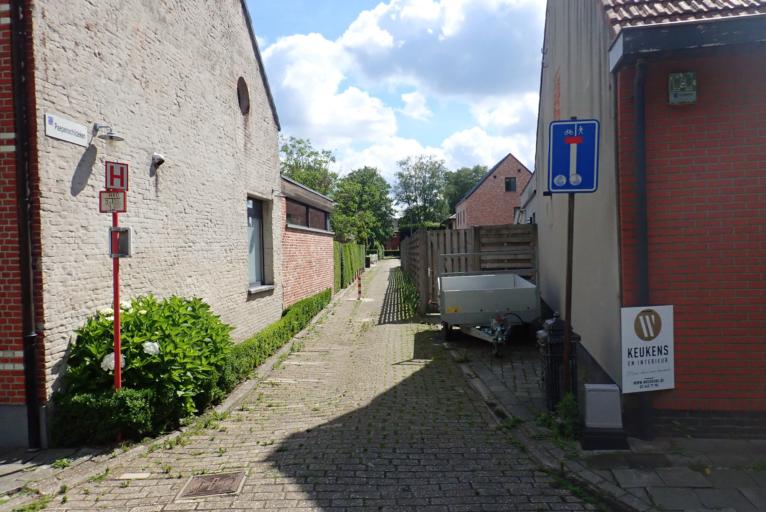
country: BE
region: Flanders
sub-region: Provincie Antwerpen
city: Oostmalle
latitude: 51.3035
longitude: 4.7301
